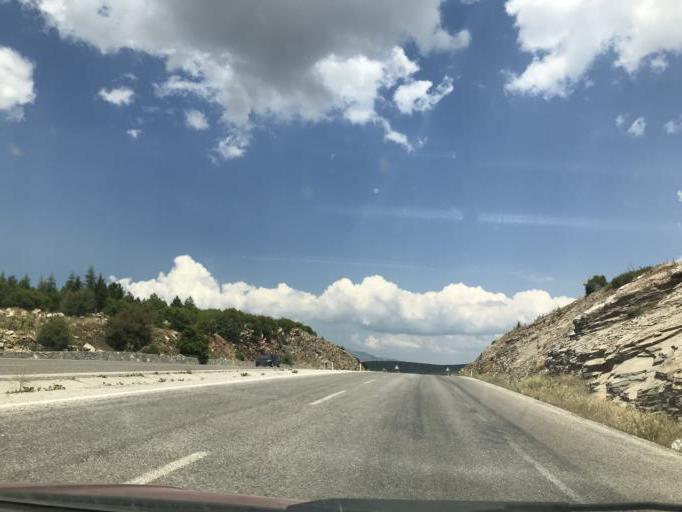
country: TR
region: Denizli
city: Tavas
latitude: 37.5933
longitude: 29.1121
